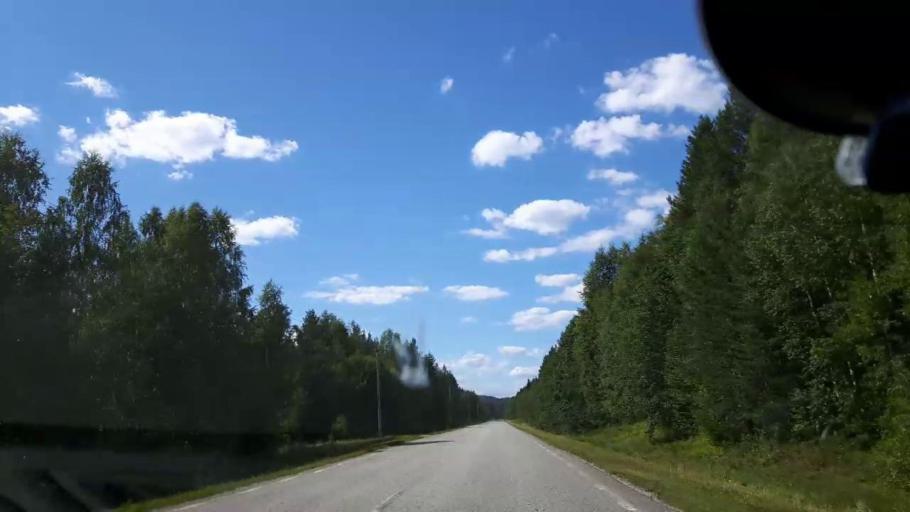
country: SE
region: Vaesternorrland
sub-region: Ange Kommun
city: Fransta
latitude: 62.7619
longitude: 16.2691
